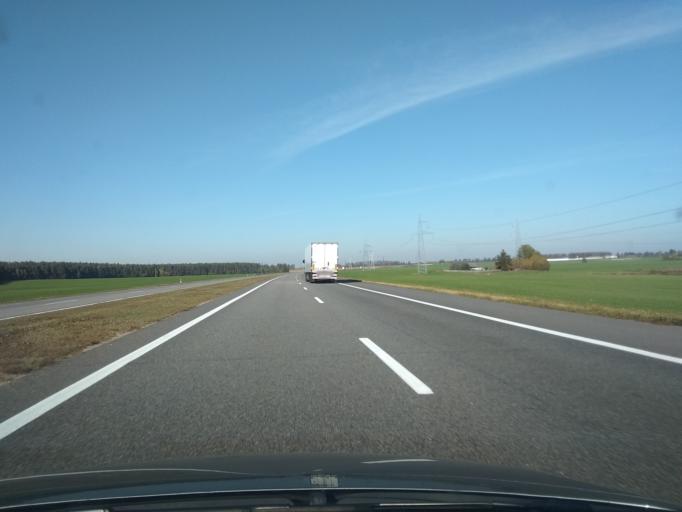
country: BY
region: Brest
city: Baranovichi
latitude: 53.0917
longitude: 25.8867
